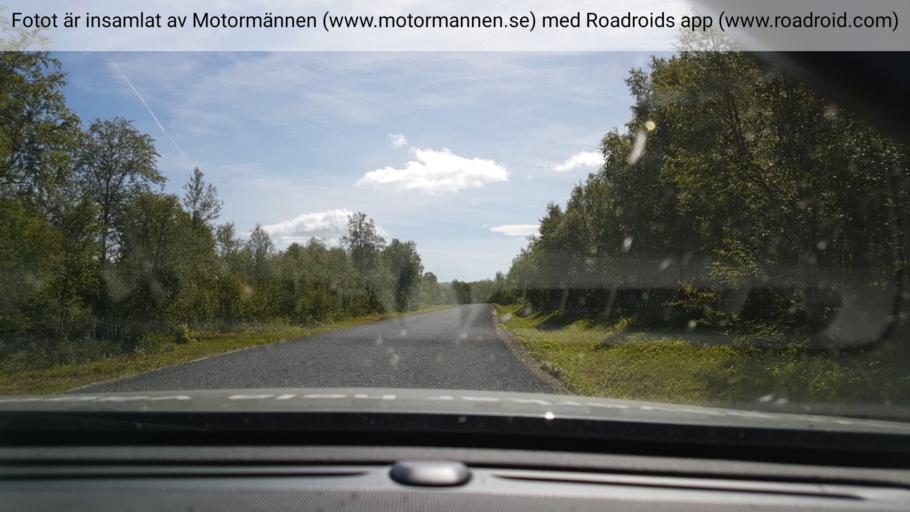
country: NO
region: Nordland
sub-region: Hattfjelldal
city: Hattfjelldal
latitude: 65.4208
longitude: 14.9155
